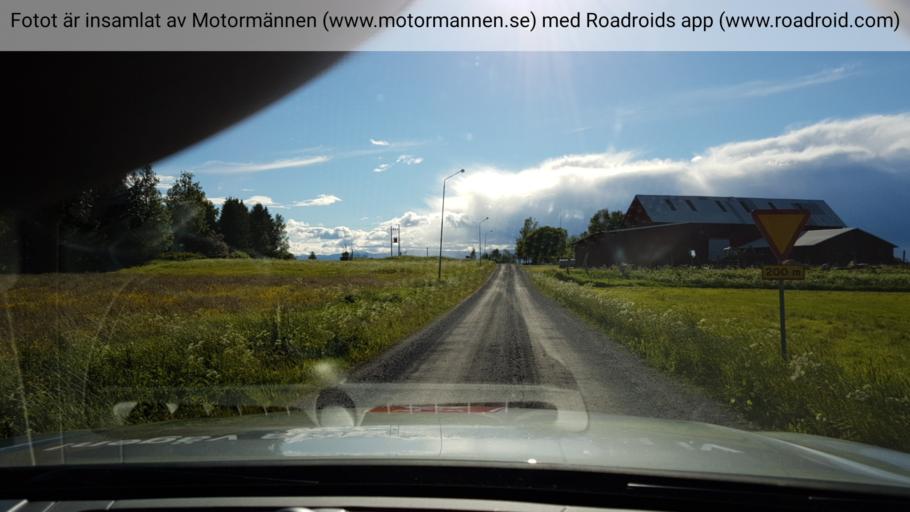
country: SE
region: Jaemtland
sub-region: Bergs Kommun
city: Hoverberg
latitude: 63.0263
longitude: 14.3753
